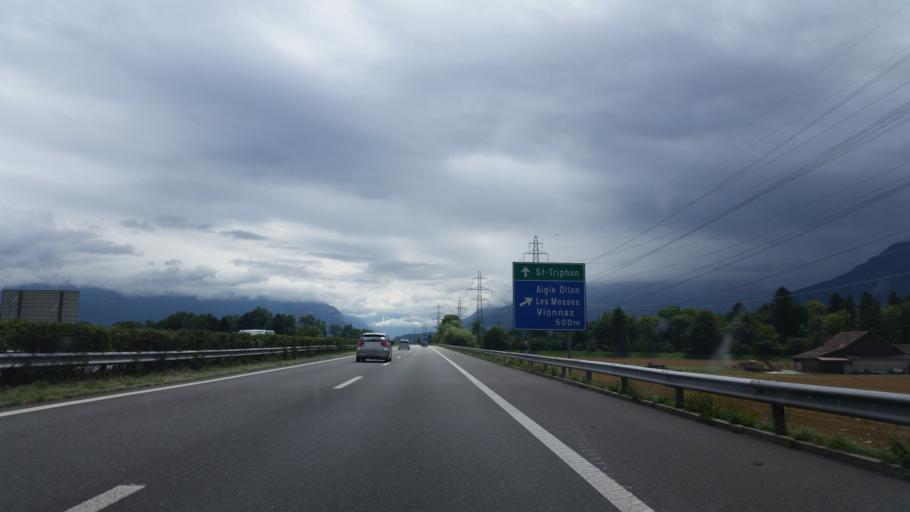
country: CH
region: Vaud
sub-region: Aigle District
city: Aigle
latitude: 46.3275
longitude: 6.9363
